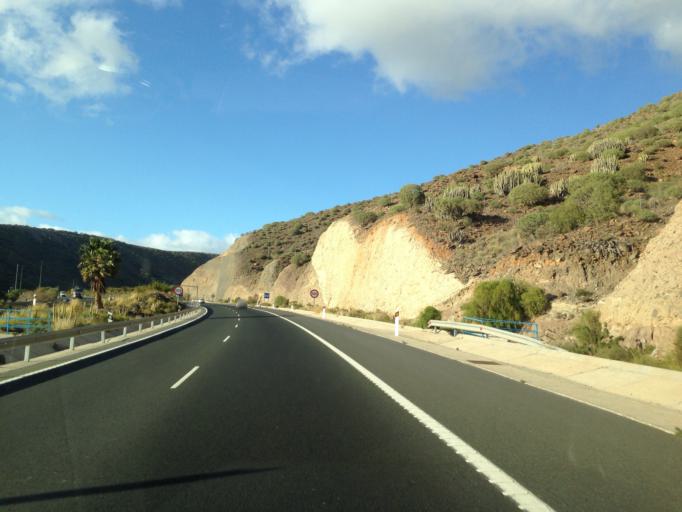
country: ES
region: Canary Islands
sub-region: Provincia de Las Palmas
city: Puerto Rico
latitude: 27.7800
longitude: -15.6771
